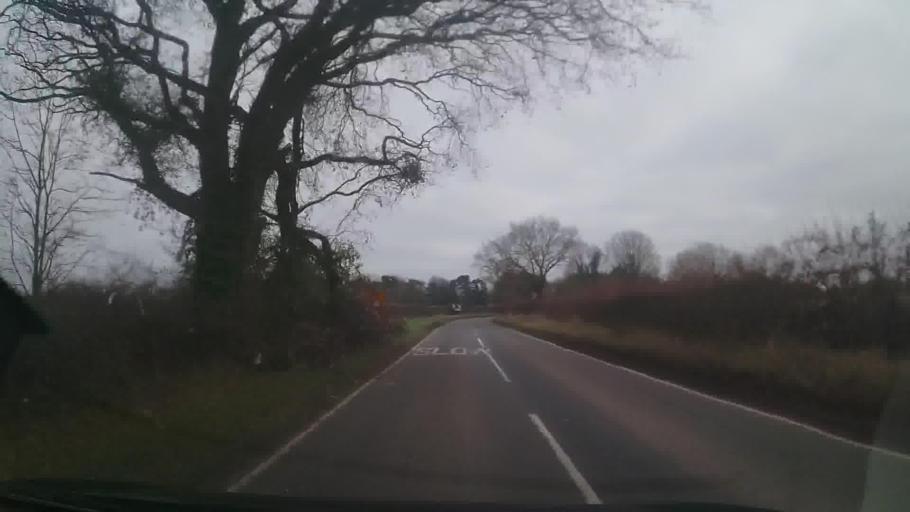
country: GB
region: England
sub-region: Shropshire
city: Great Ness
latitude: 52.7825
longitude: -2.8480
